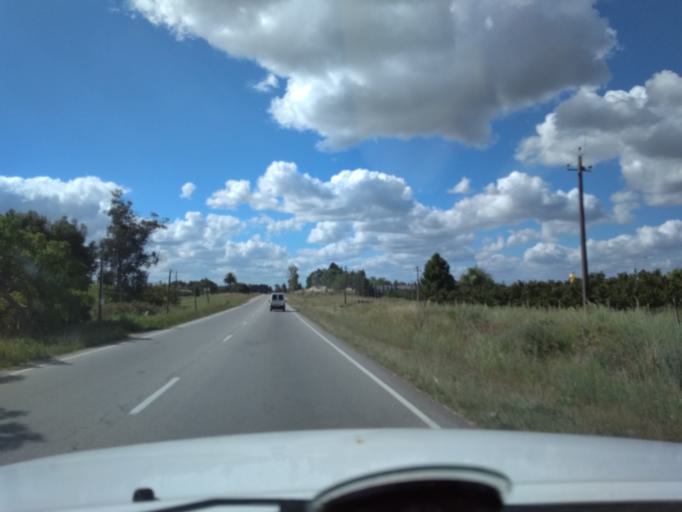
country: UY
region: Canelones
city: Sauce
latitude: -34.6818
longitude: -56.0525
